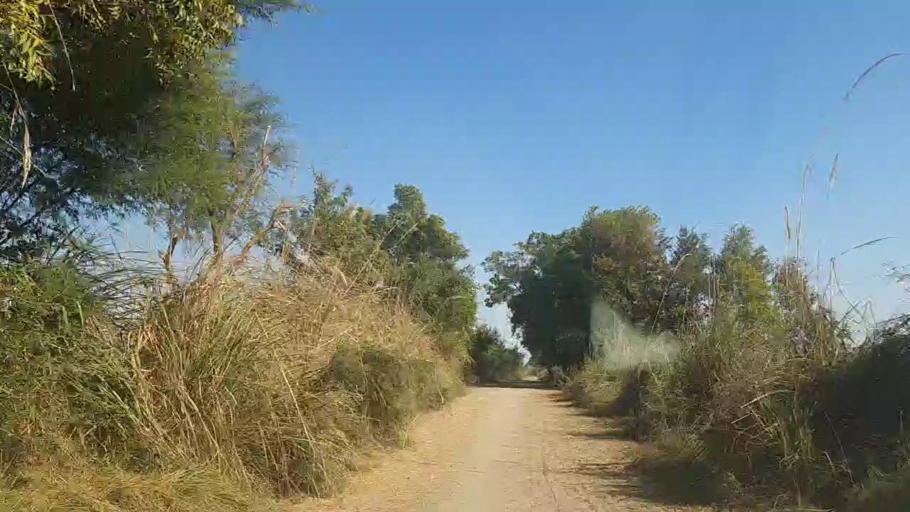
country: PK
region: Sindh
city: Sanghar
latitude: 26.2204
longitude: 68.9684
